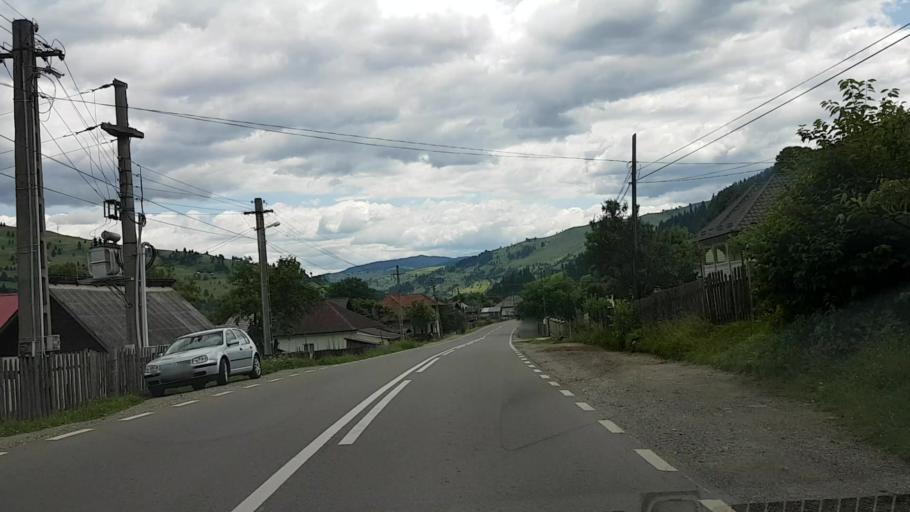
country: RO
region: Neamt
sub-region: Comuna Borca
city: Borca
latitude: 47.1906
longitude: 25.7714
